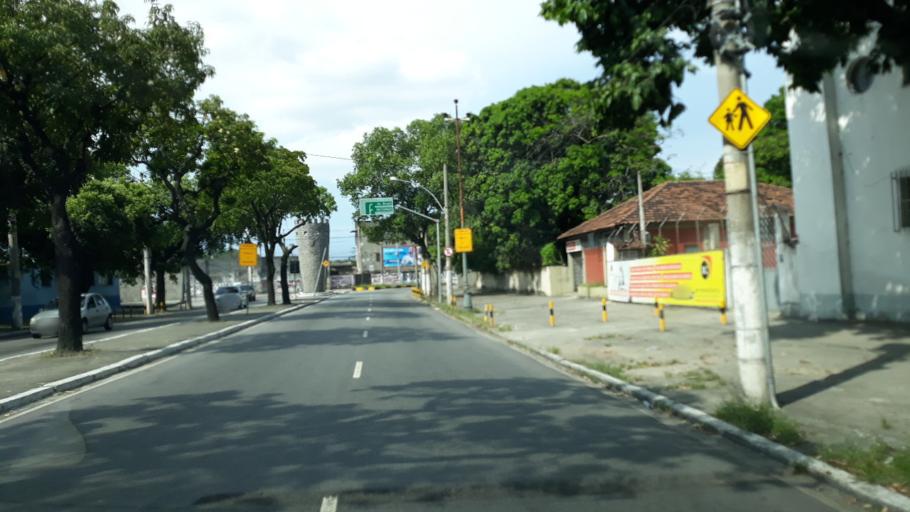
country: BR
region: Rio de Janeiro
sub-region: Sao Joao De Meriti
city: Sao Joao de Meriti
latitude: -22.8557
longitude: -43.3858
